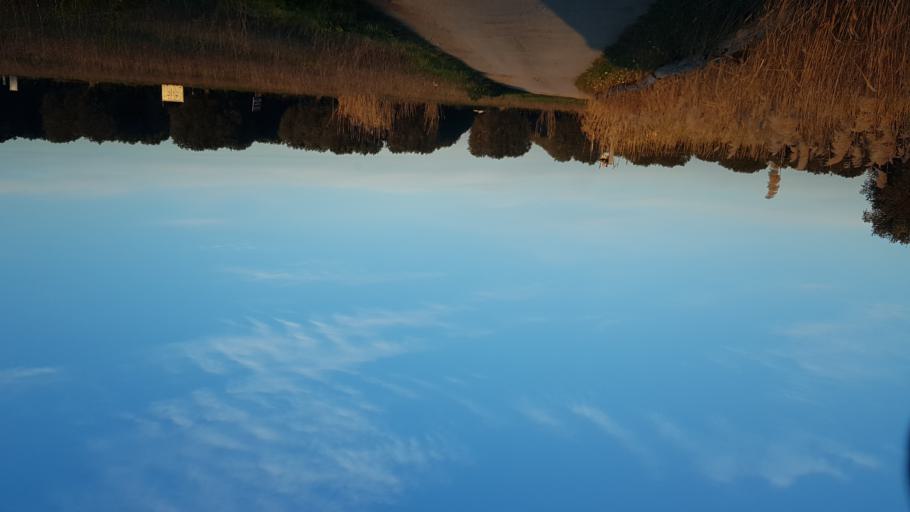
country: IT
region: Apulia
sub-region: Provincia di Brindisi
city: Tuturano
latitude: 40.5495
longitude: 17.9464
